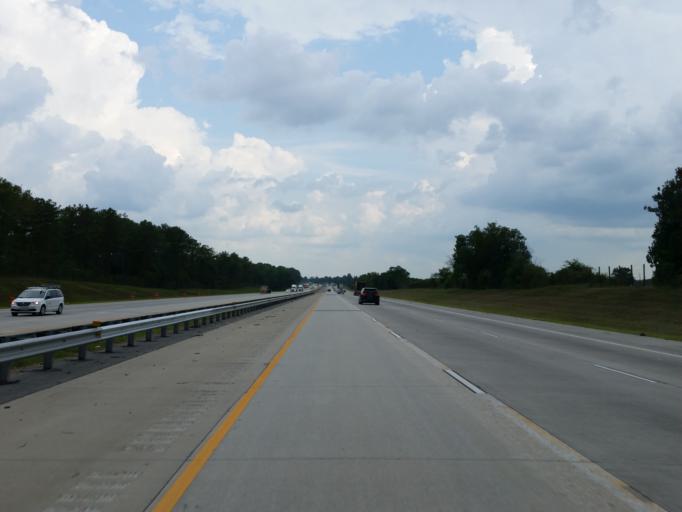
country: US
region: Georgia
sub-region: Dooly County
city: Unadilla
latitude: 32.3081
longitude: -83.7628
